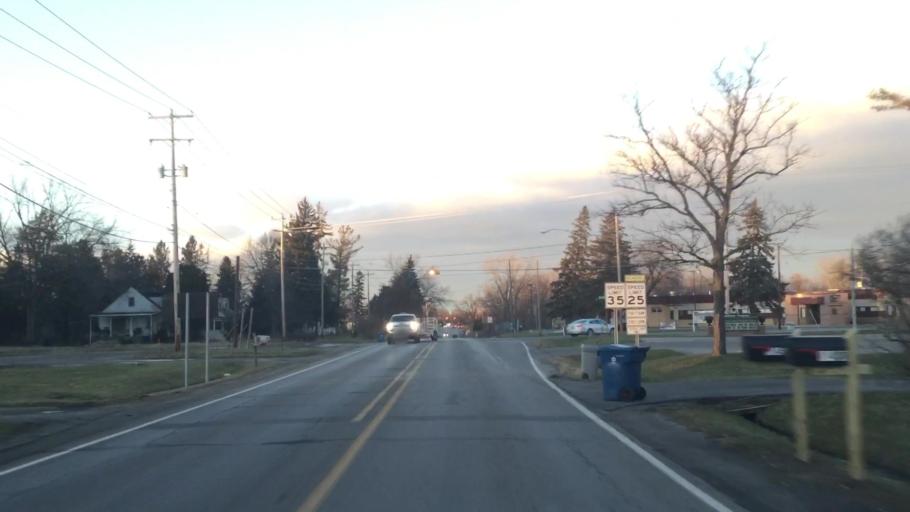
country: US
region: Michigan
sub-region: Genesee County
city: Lake Fenton
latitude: 42.8578
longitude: -83.7292
